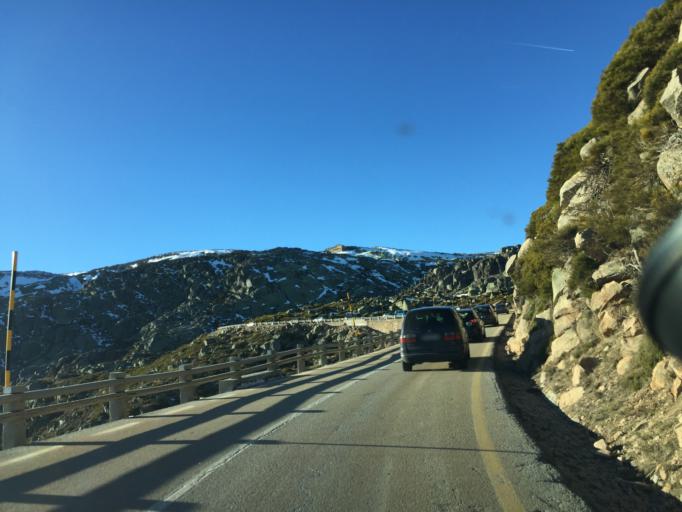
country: PT
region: Castelo Branco
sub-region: Covilha
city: Covilha
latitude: 40.3203
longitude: -7.5995
